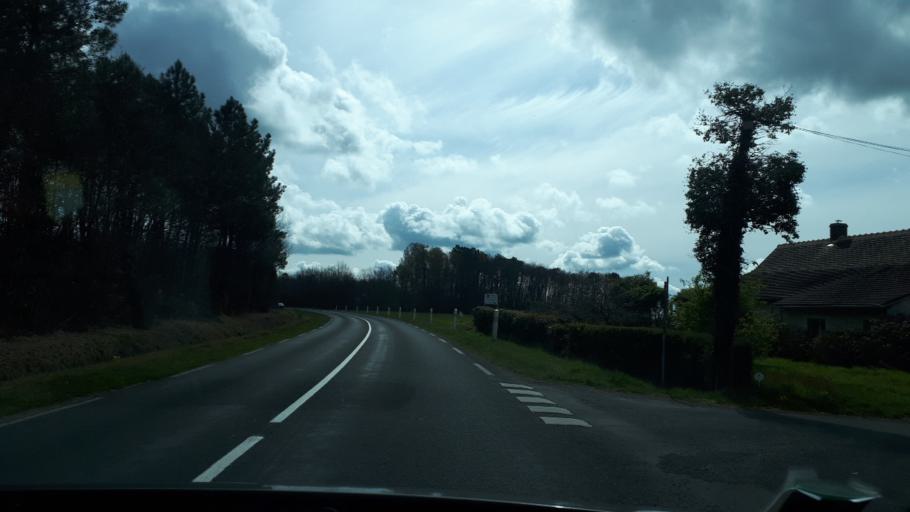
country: FR
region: Pays de la Loire
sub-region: Departement de la Sarthe
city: Le Grand-Luce
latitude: 47.8756
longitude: 0.4323
